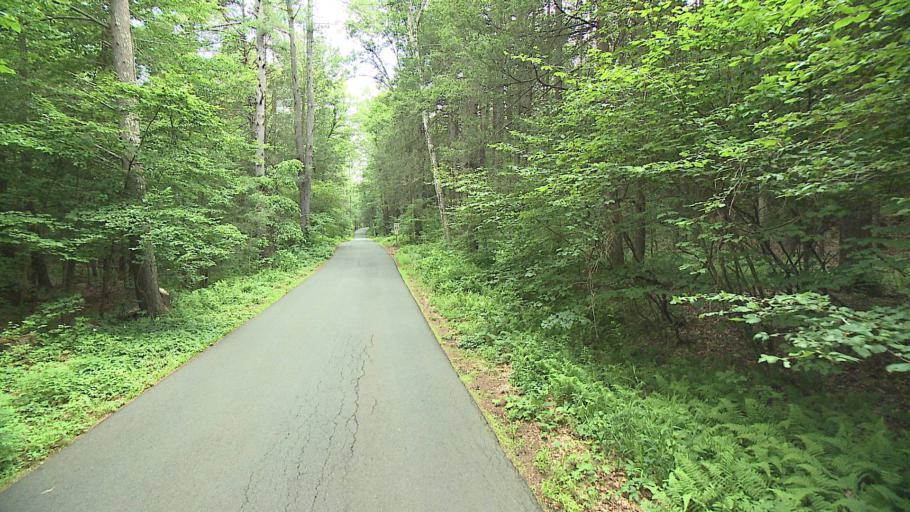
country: US
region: Connecticut
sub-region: Litchfield County
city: New Hartford Center
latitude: 41.9302
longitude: -72.9999
